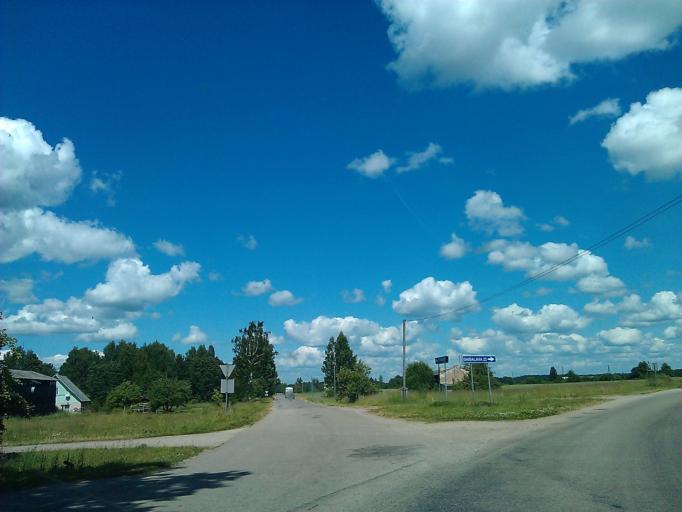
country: LV
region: Vilanu
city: Vilani
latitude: 56.5703
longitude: 26.9320
